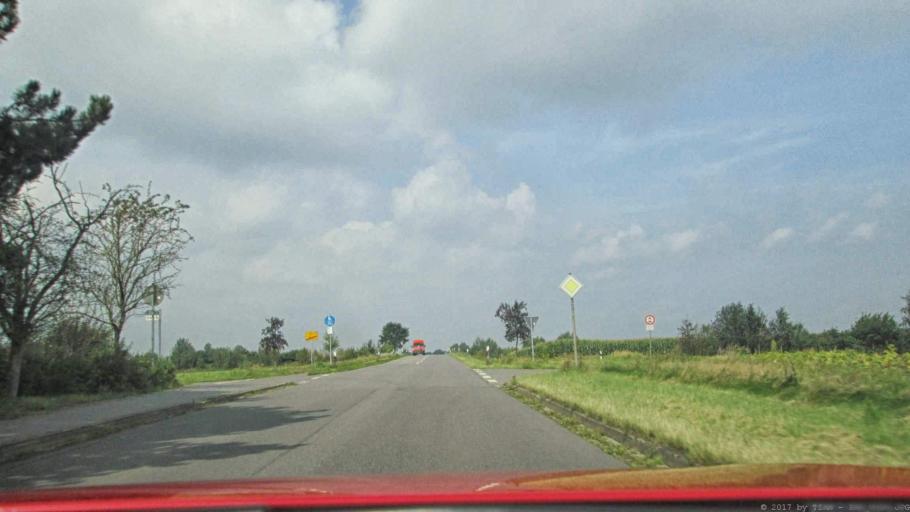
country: DE
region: Lower Saxony
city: Uelzen
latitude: 52.9415
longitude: 10.5769
